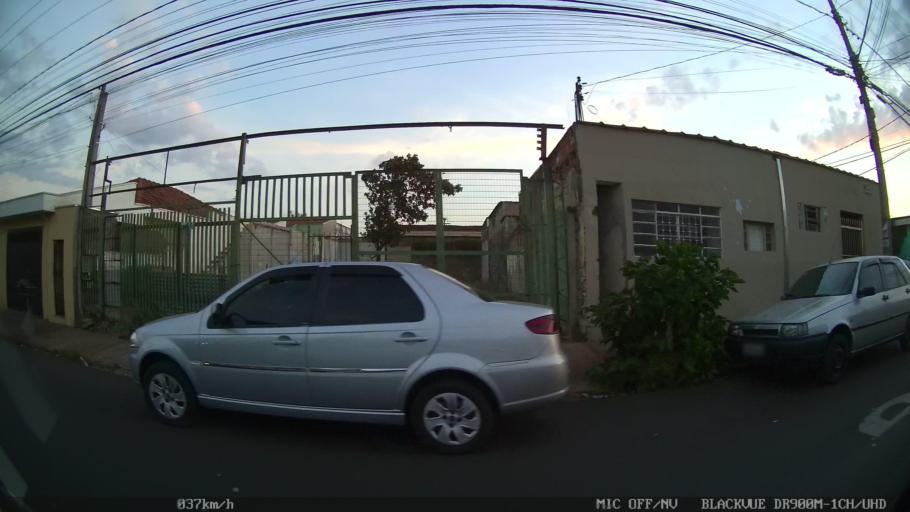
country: BR
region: Sao Paulo
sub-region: Ribeirao Preto
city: Ribeirao Preto
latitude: -21.1499
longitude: -47.8140
